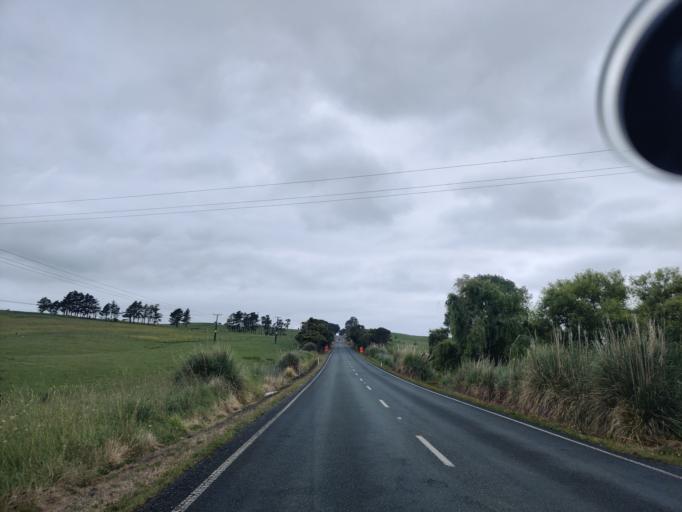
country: NZ
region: Northland
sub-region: Kaipara District
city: Dargaville
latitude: -36.1282
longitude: 174.1270
